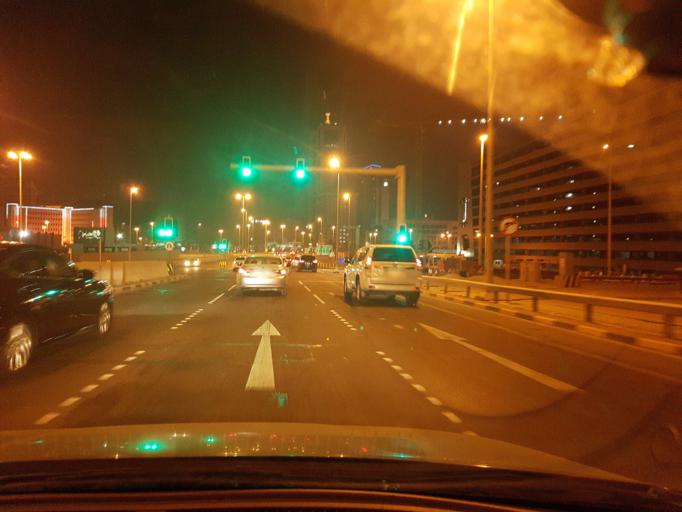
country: BH
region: Manama
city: Manama
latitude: 26.2404
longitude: 50.5753
